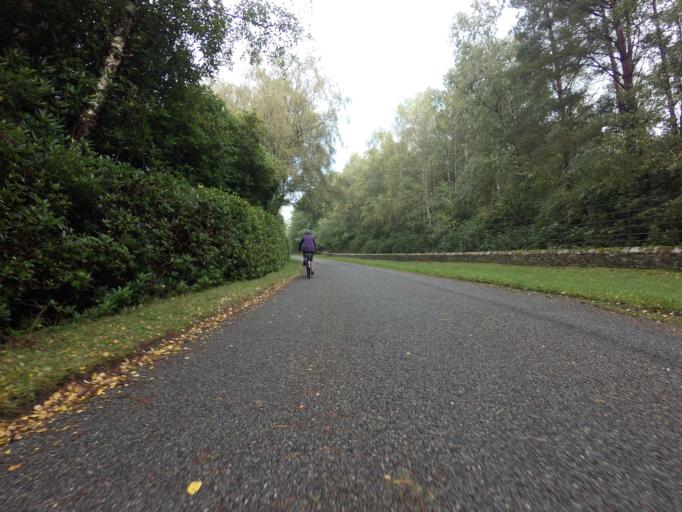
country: GB
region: England
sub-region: Norfolk
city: Dersingham
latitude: 52.8219
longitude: 0.4965
